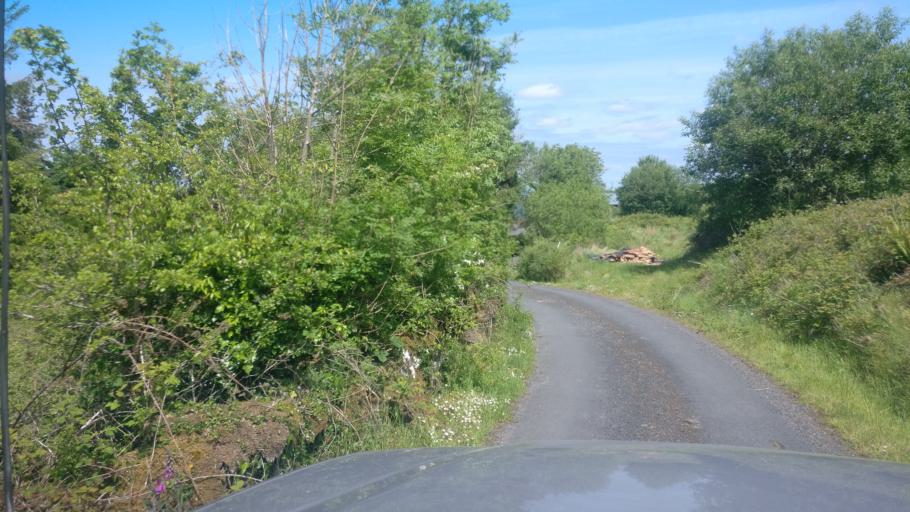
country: IE
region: Connaught
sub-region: County Galway
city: Gort
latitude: 53.1262
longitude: -8.7032
